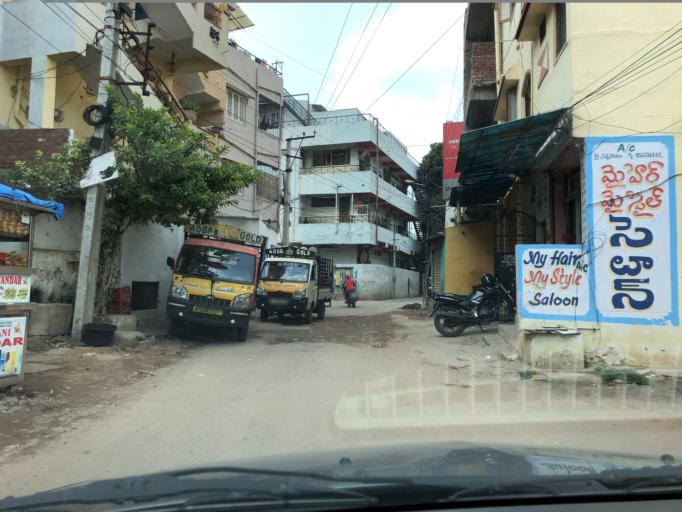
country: IN
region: Telangana
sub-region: Hyderabad
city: Malkajgiri
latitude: 17.4465
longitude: 78.4778
